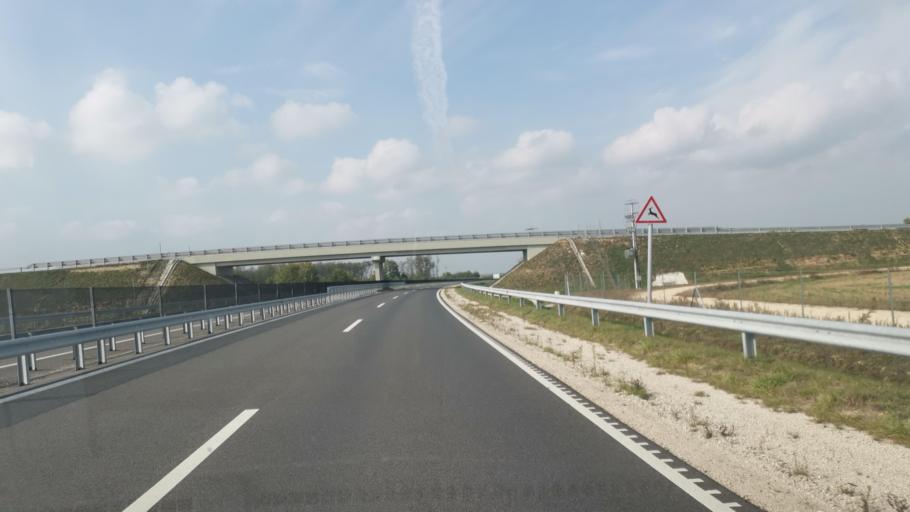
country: HU
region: Gyor-Moson-Sopron
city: Fertoszentmiklos
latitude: 47.5572
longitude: 16.8729
